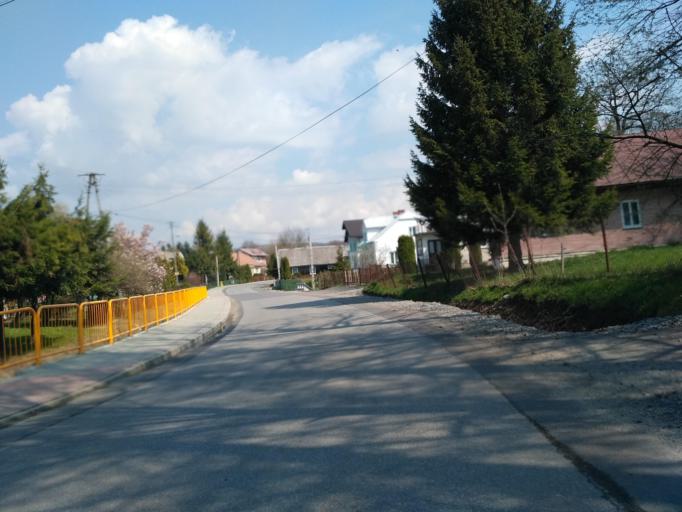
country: PL
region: Subcarpathian Voivodeship
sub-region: Powiat sanocki
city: Zarszyn
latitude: 49.6170
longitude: 22.0174
